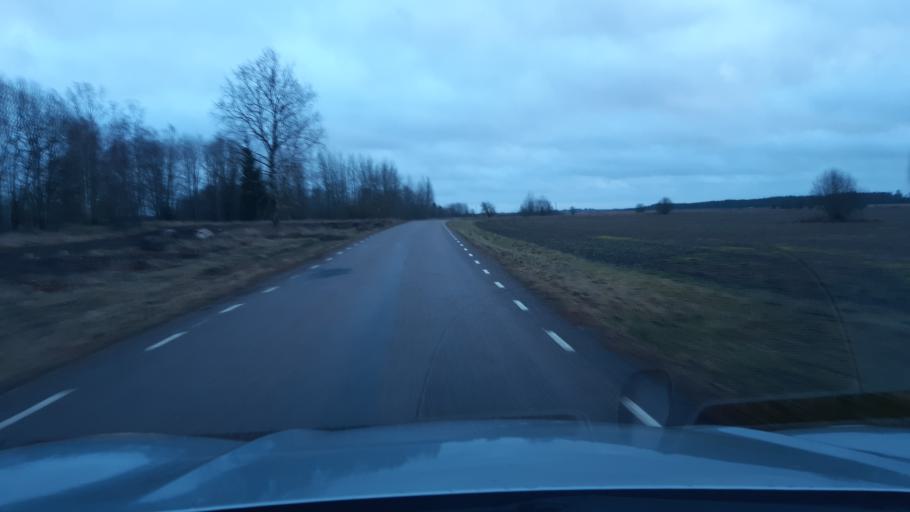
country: EE
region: Raplamaa
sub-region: Rapla vald
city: Rapla
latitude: 59.0064
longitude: 24.7117
